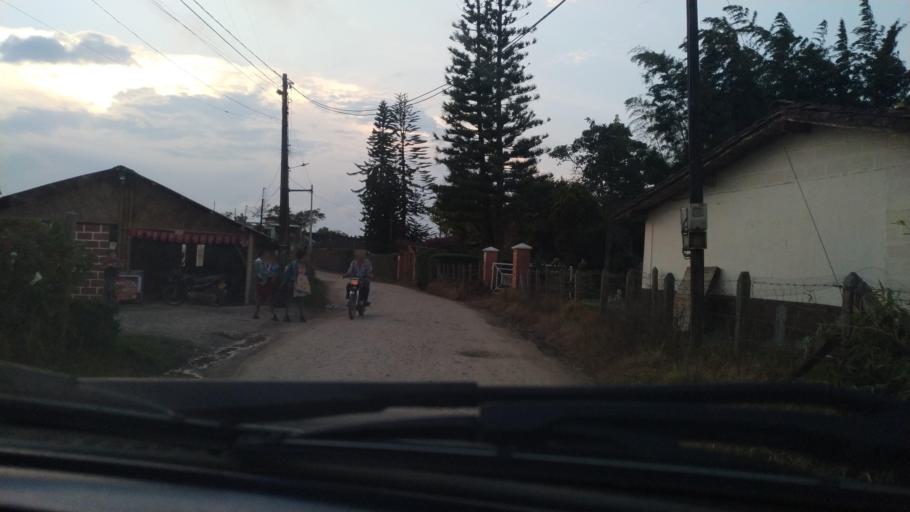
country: CO
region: Antioquia
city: Marinilla
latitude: 6.1938
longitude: -75.2839
